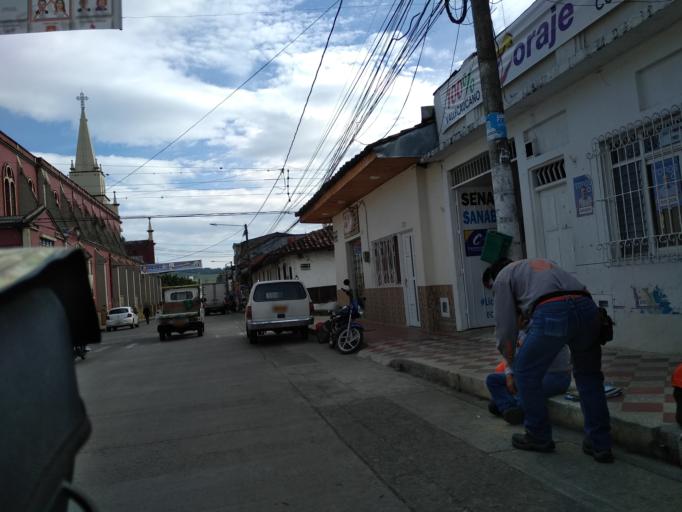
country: CO
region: Valle del Cauca
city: Caicedonia
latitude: 4.3305
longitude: -75.8284
